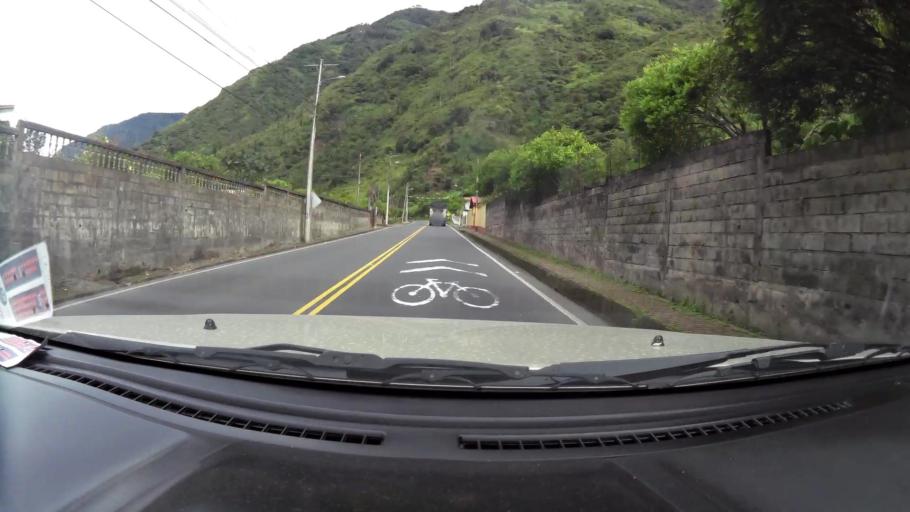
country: EC
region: Tungurahua
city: Banos
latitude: -1.3976
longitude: -78.3860
